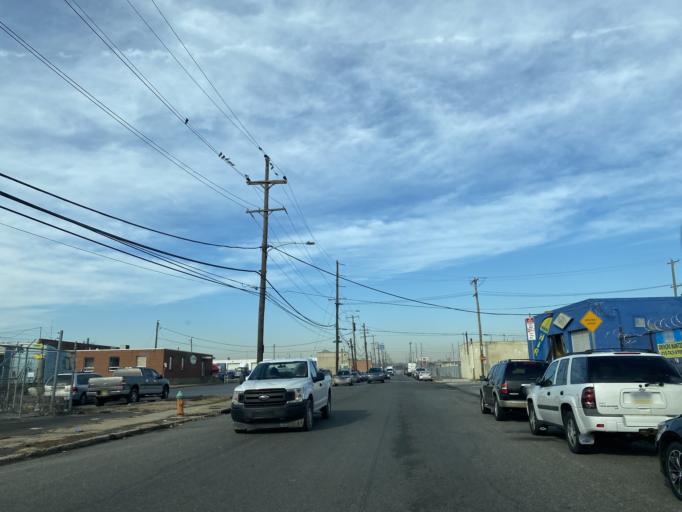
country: US
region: New Jersey
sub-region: Camden County
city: Pennsauken
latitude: 39.9939
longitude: -75.0870
